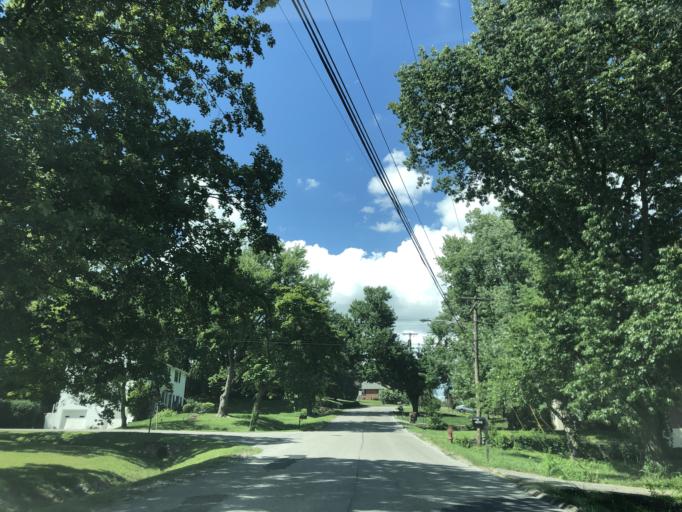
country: US
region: Tennessee
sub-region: Davidson County
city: Oak Hill
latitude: 36.0748
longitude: -86.7346
